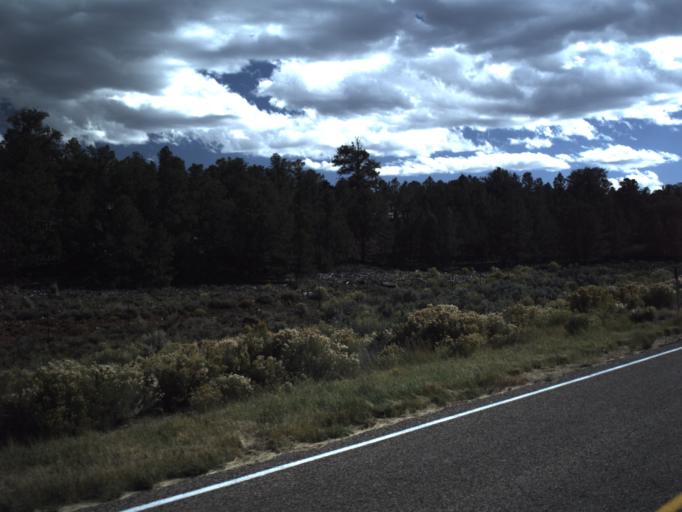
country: US
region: Utah
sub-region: Garfield County
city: Panguitch
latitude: 37.7764
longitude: -112.4430
